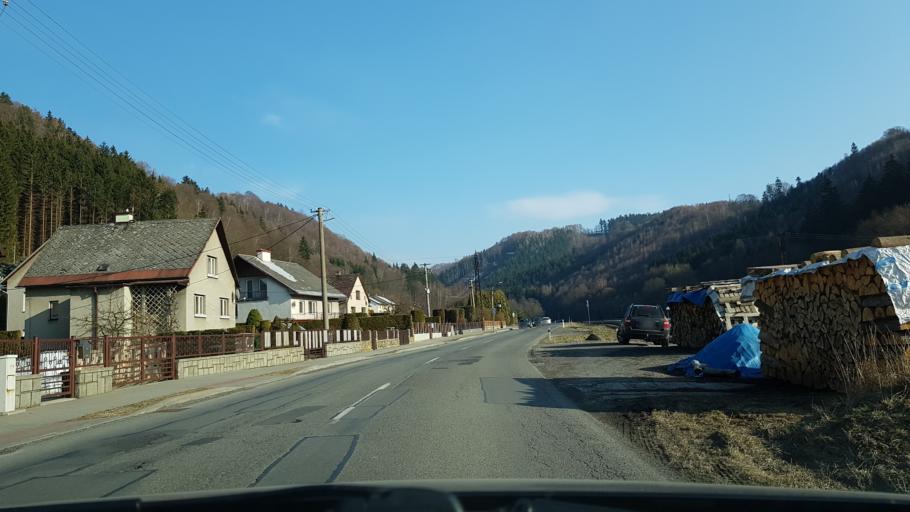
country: CZ
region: Olomoucky
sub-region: Okres Sumperk
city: Hanusovice
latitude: 50.0803
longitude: 16.9418
